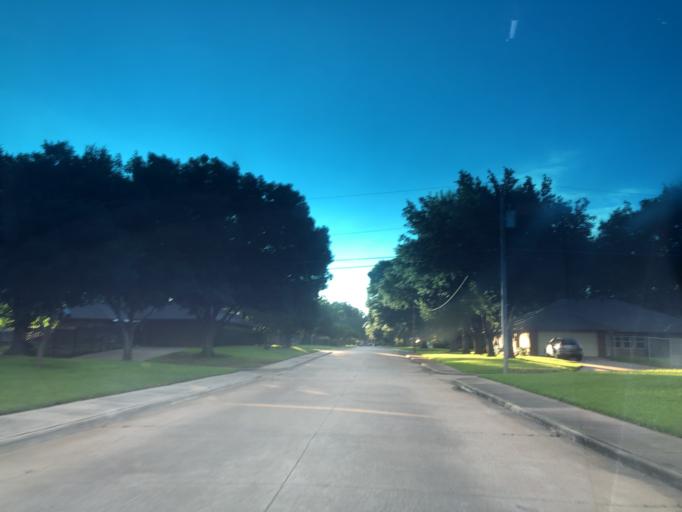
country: US
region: Texas
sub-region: Dallas County
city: Grand Prairie
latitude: 32.7817
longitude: -97.0366
